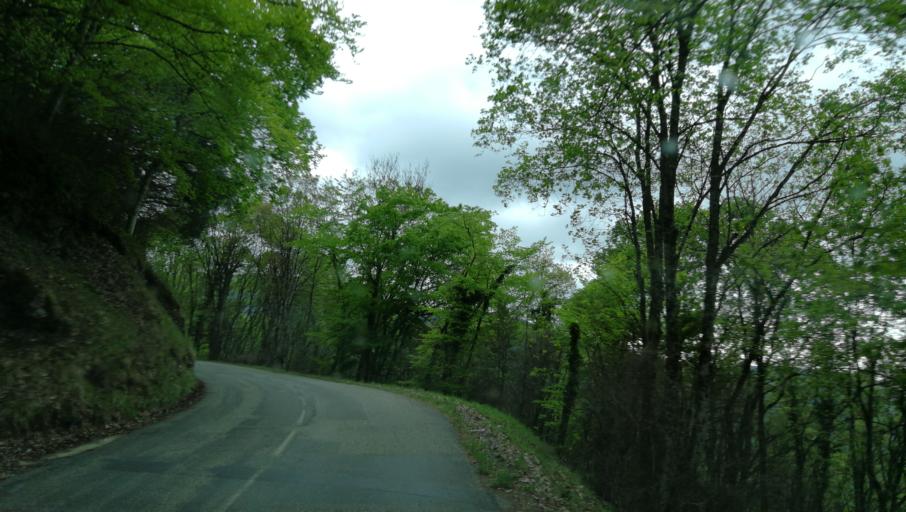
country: FR
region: Rhone-Alpes
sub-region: Departement de la Drome
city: Saint-Jean-en-Royans
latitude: 44.9983
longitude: 5.2939
